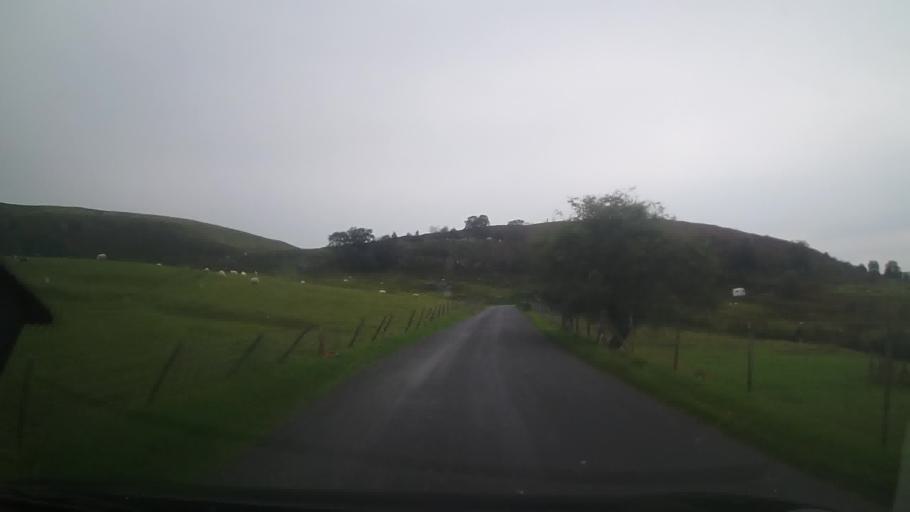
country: GB
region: Wales
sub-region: Sir Powys
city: Rhayader
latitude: 52.2927
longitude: -3.6146
